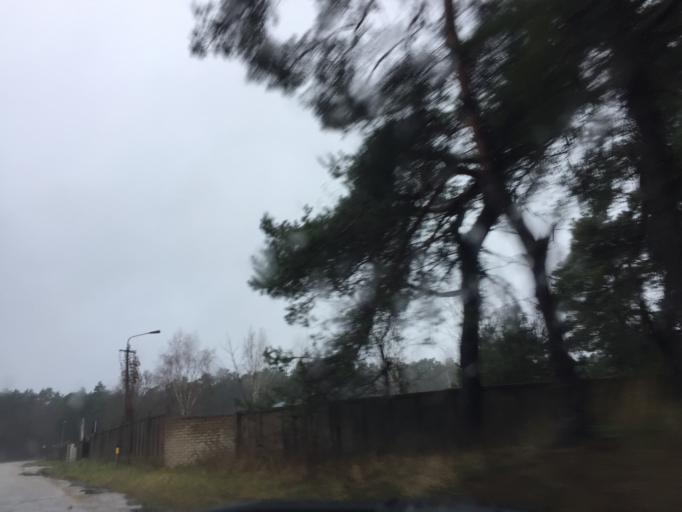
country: LV
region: Jekabpils Rajons
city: Jekabpils
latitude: 56.4904
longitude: 25.8485
